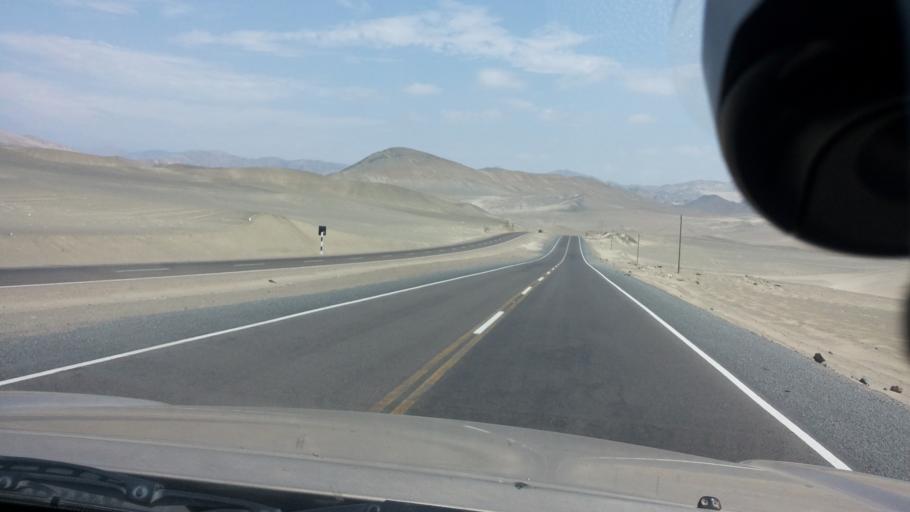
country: PE
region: Ancash
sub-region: Provincia de Huarmey
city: La Caleta Culebras
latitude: -9.7700
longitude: -78.2359
